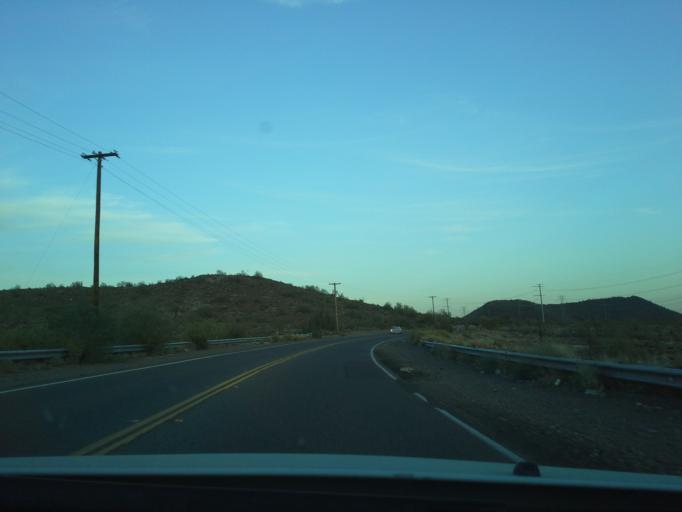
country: US
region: Arizona
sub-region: Maricopa County
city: Cave Creek
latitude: 33.7128
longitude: -112.0699
